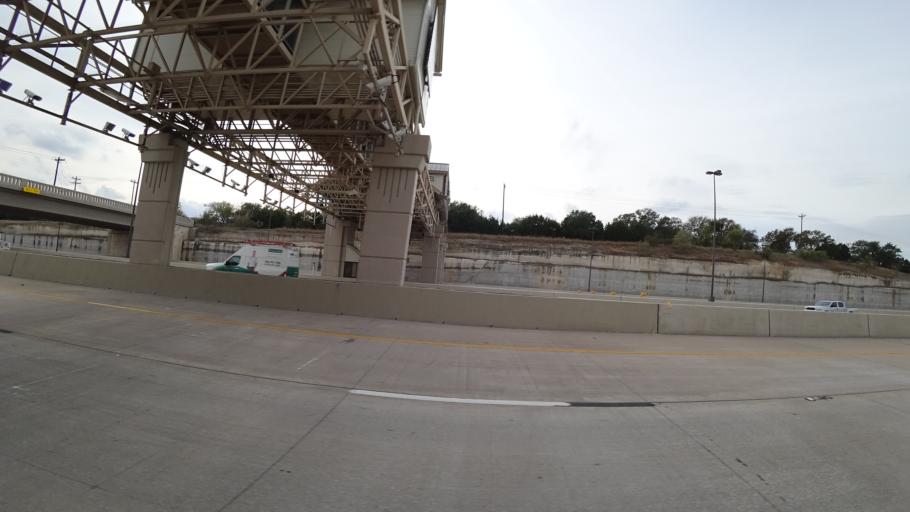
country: US
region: Texas
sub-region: Williamson County
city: Cedar Park
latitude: 30.5143
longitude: -97.8131
